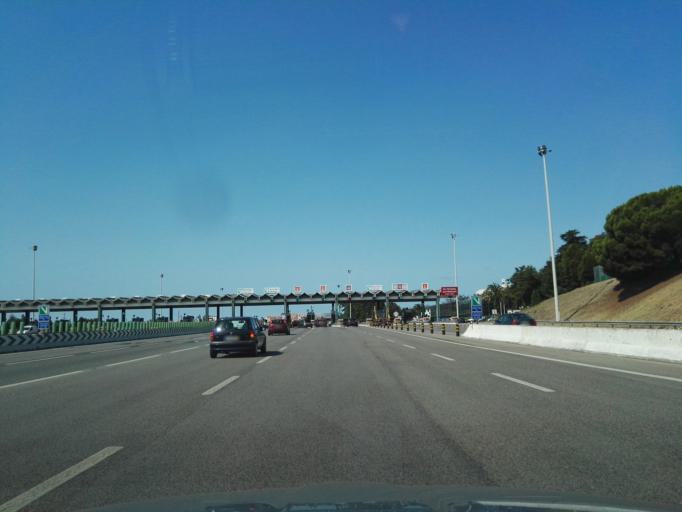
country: PT
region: Lisbon
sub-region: Cascais
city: Sao Domingos de Rana
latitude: 38.7081
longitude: -9.3331
